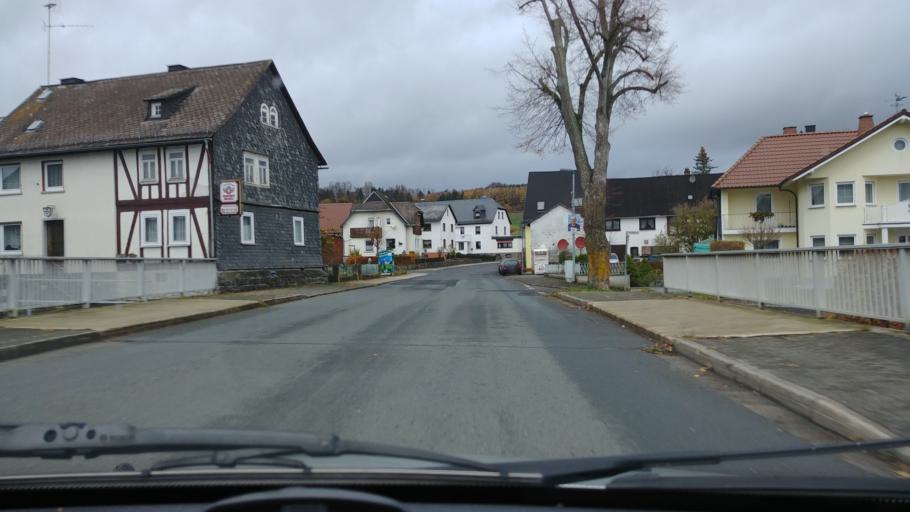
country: DE
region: Hesse
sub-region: Regierungsbezirk Giessen
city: Driedorf
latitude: 50.6186
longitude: 8.1920
